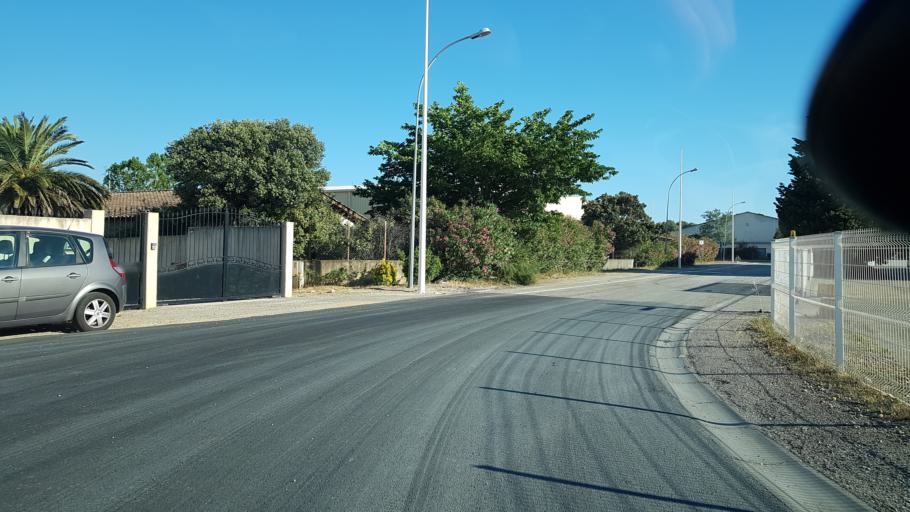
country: FR
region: Provence-Alpes-Cote d'Azur
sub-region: Departement des Bouches-du-Rhone
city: Saint-Martin-de-Crau
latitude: 43.6237
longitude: 4.7879
